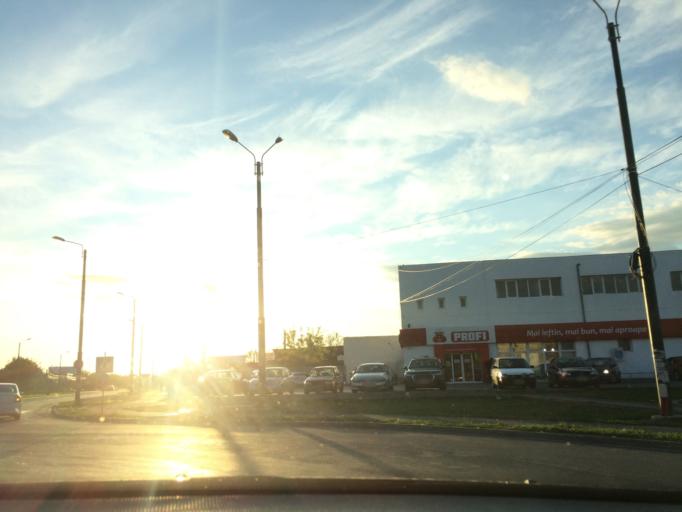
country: RO
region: Timis
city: Timisoara
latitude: 45.7668
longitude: 21.1955
